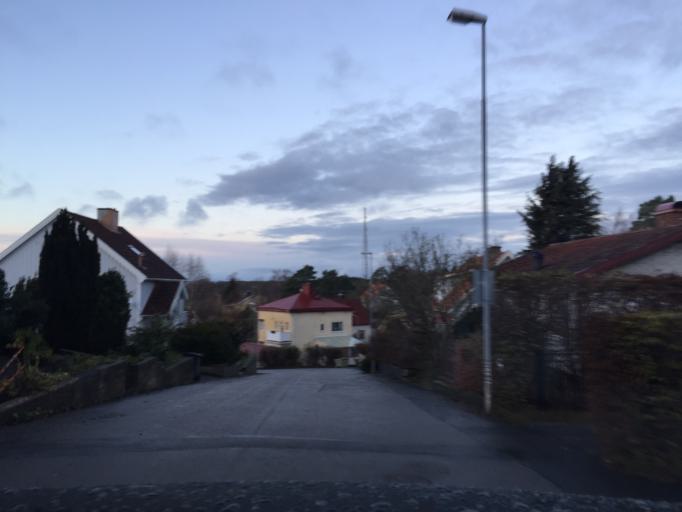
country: SE
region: Blekinge
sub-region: Karlshamns Kommun
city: Karlshamn
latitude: 56.1713
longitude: 14.8770
